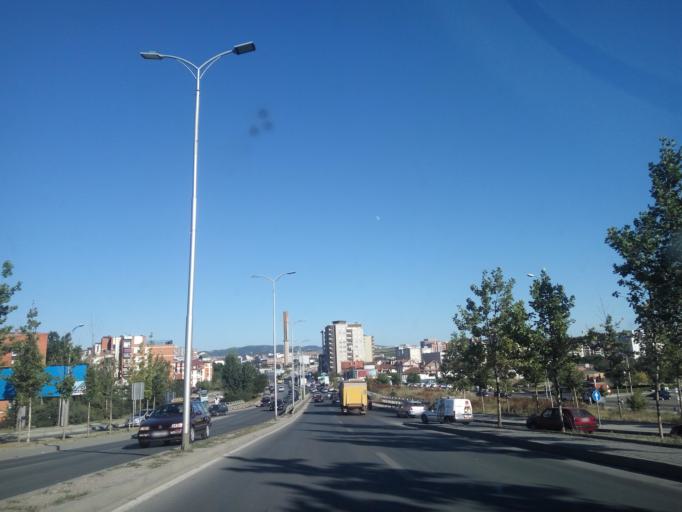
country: XK
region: Pristina
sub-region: Komuna e Prishtines
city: Pristina
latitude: 42.6519
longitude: 21.1469
